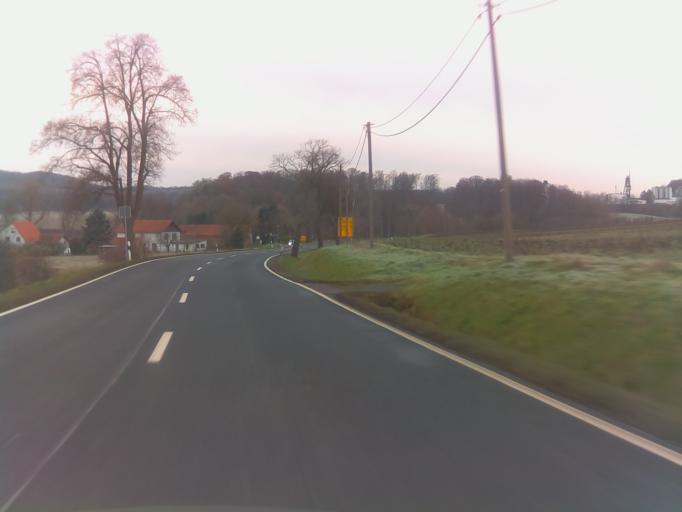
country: DE
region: Thuringia
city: Unterbreizbach
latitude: 50.7880
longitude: 9.9943
